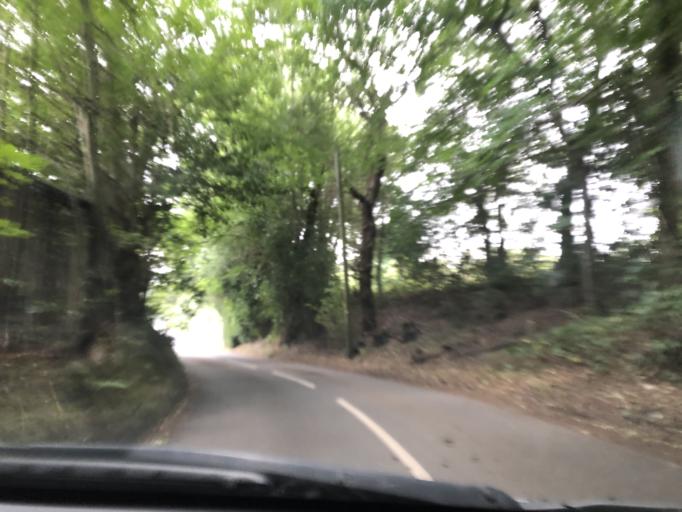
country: GB
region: England
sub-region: Kent
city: Westerham
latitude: 51.2426
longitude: 0.0809
